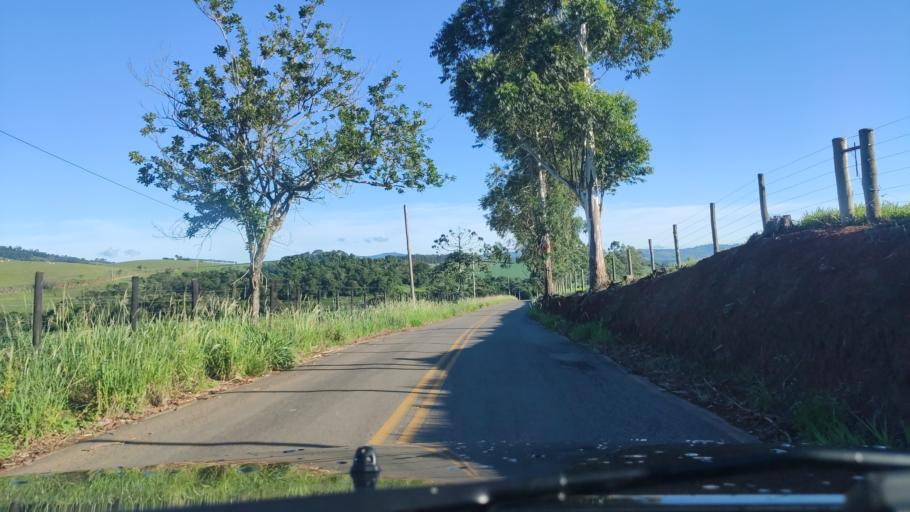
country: BR
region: Sao Paulo
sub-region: Serra Negra
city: Serra Negra
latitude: -22.5793
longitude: -46.6222
